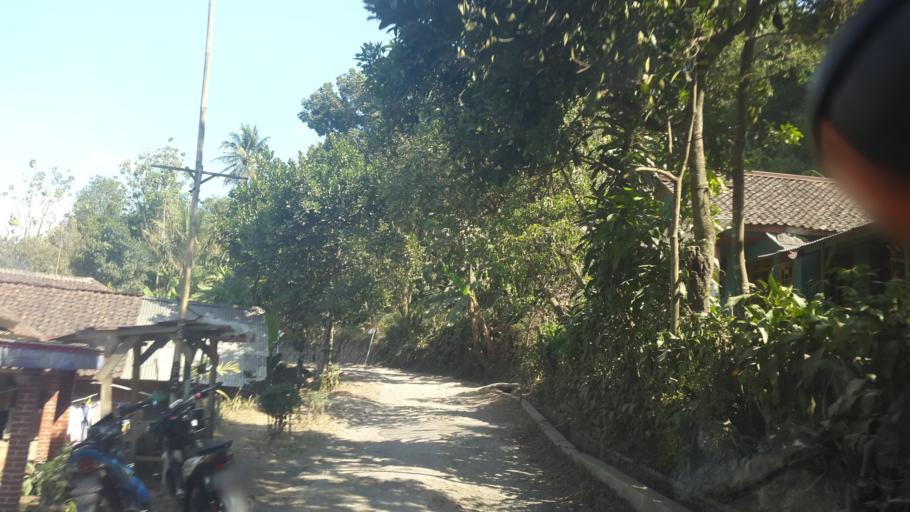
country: ID
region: West Java
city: Suryabakti
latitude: -6.9949
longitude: 106.8464
